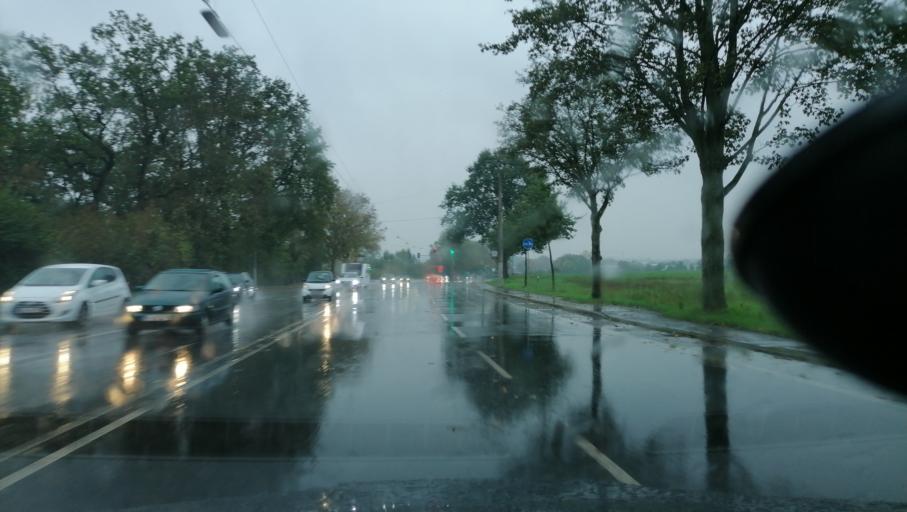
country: DE
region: North Rhine-Westphalia
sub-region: Regierungsbezirk Munster
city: Recklinghausen
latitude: 51.5891
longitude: 7.1814
